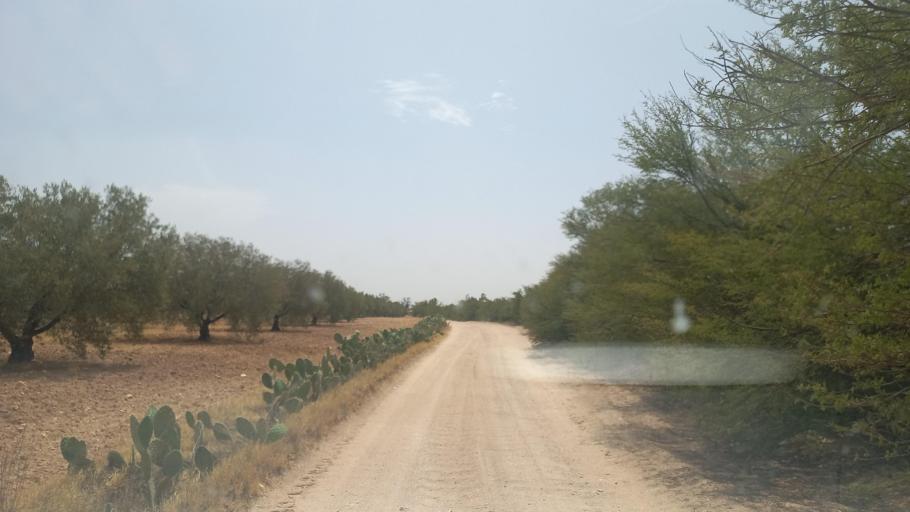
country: TN
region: Al Qasrayn
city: Kasserine
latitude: 35.2555
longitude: 9.0065
